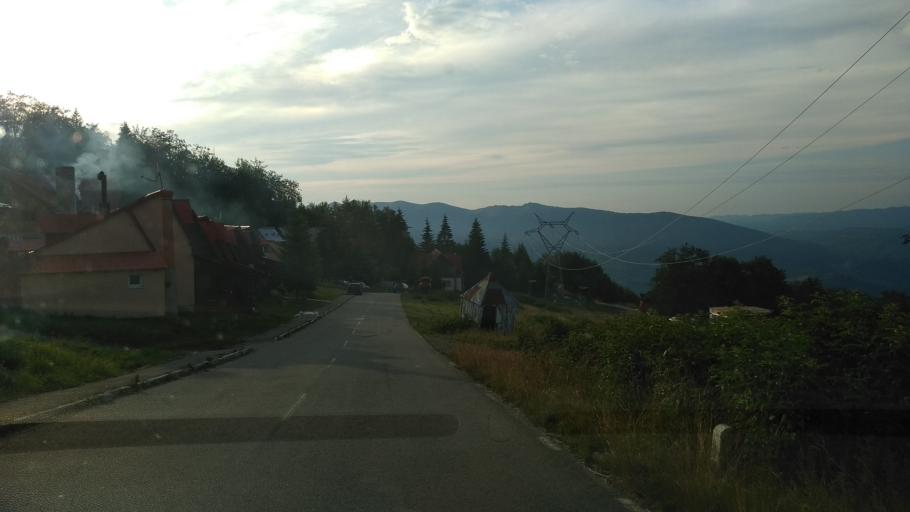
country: RO
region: Hunedoara
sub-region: Municipiul  Vulcan
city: Jiu-Paroseni
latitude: 45.3279
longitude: 23.2884
